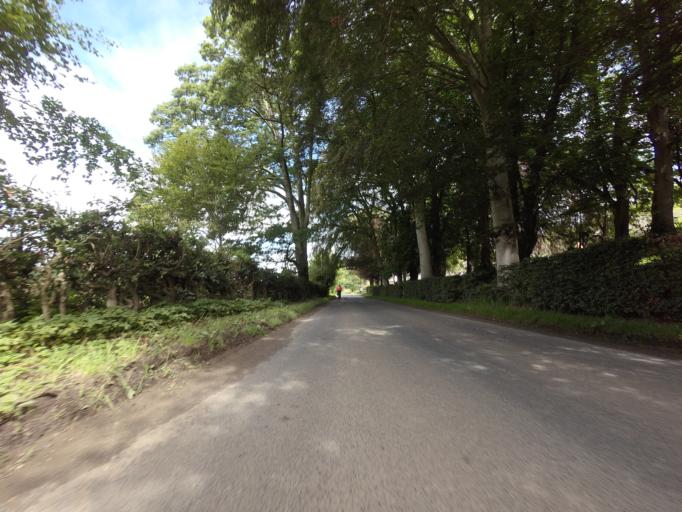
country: GB
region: Scotland
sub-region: Aberdeenshire
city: Turriff
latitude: 57.5475
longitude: -2.4820
